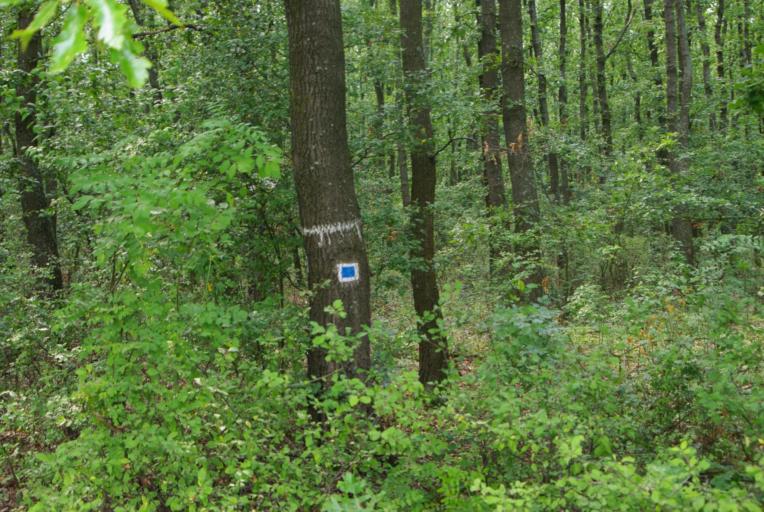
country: HU
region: Nograd
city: Bujak
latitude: 47.9330
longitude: 19.6085
